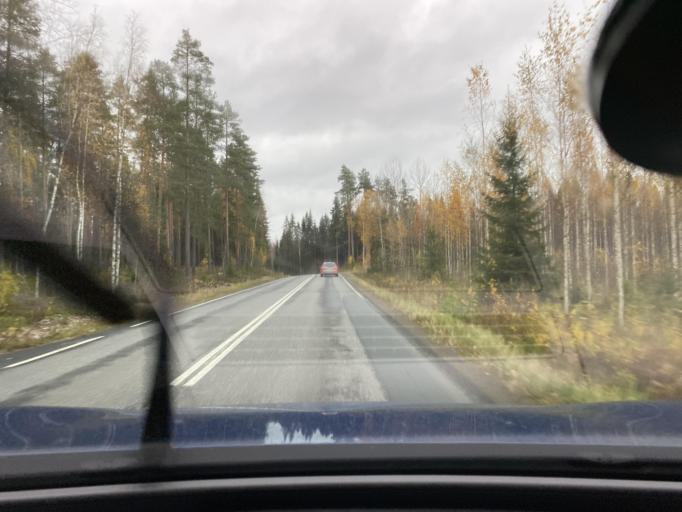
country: FI
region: Satakunta
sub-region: Pori
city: Huittinen
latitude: 61.1053
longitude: 22.5617
